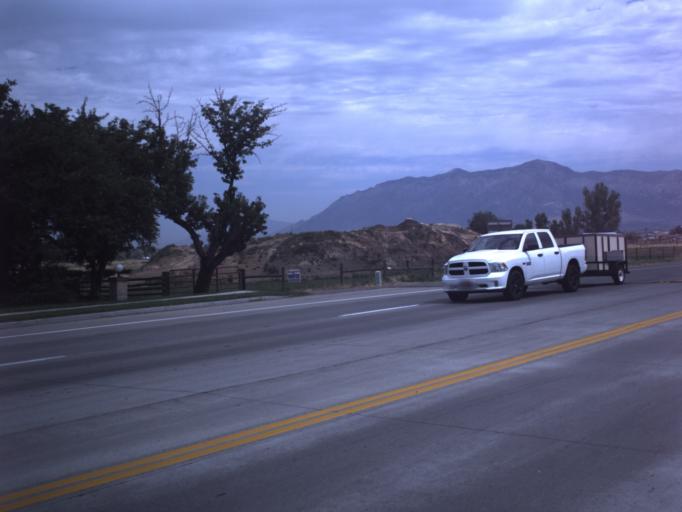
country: US
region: Utah
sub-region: Weber County
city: West Haven
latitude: 41.1985
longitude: -112.0389
